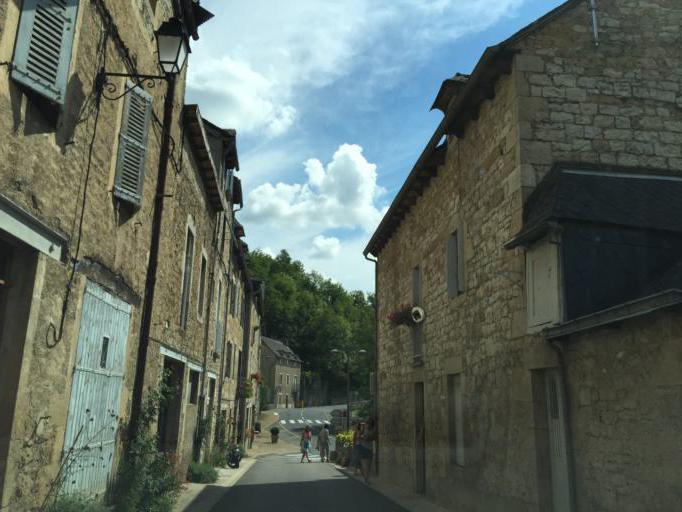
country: FR
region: Midi-Pyrenees
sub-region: Departement de l'Aveyron
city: Salles-la-Source
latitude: 44.4362
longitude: 2.5148
